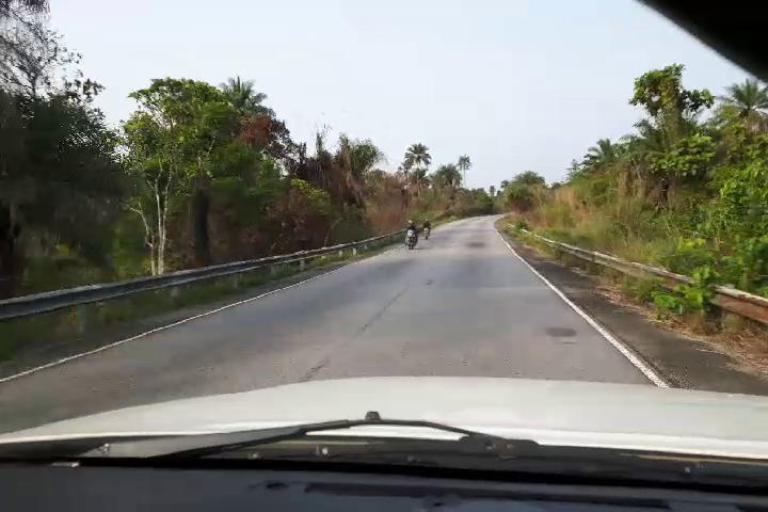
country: SL
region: Eastern Province
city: Blama
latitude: 7.9407
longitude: -11.5044
